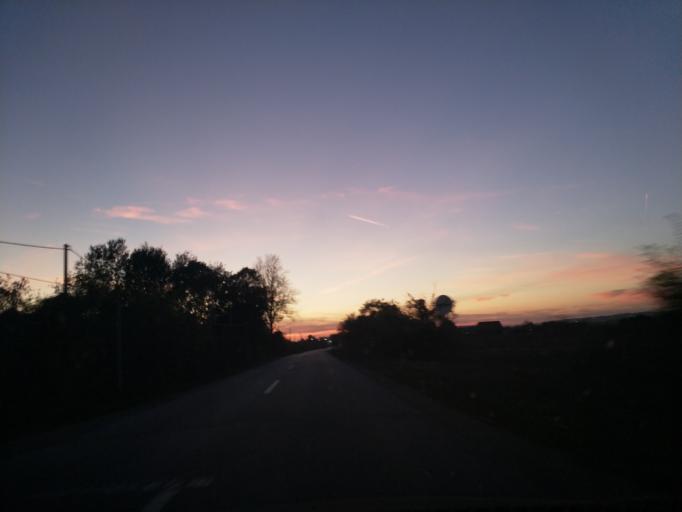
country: RS
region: Central Serbia
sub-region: Sumadijski Okrug
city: Lapovo
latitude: 44.2377
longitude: 21.1302
